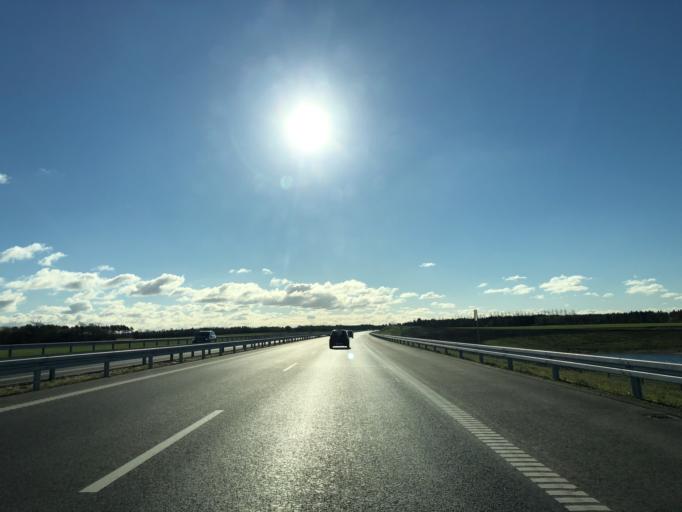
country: DK
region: Central Jutland
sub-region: Herning Kommune
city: Avlum
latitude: 56.3475
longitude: 8.7376
